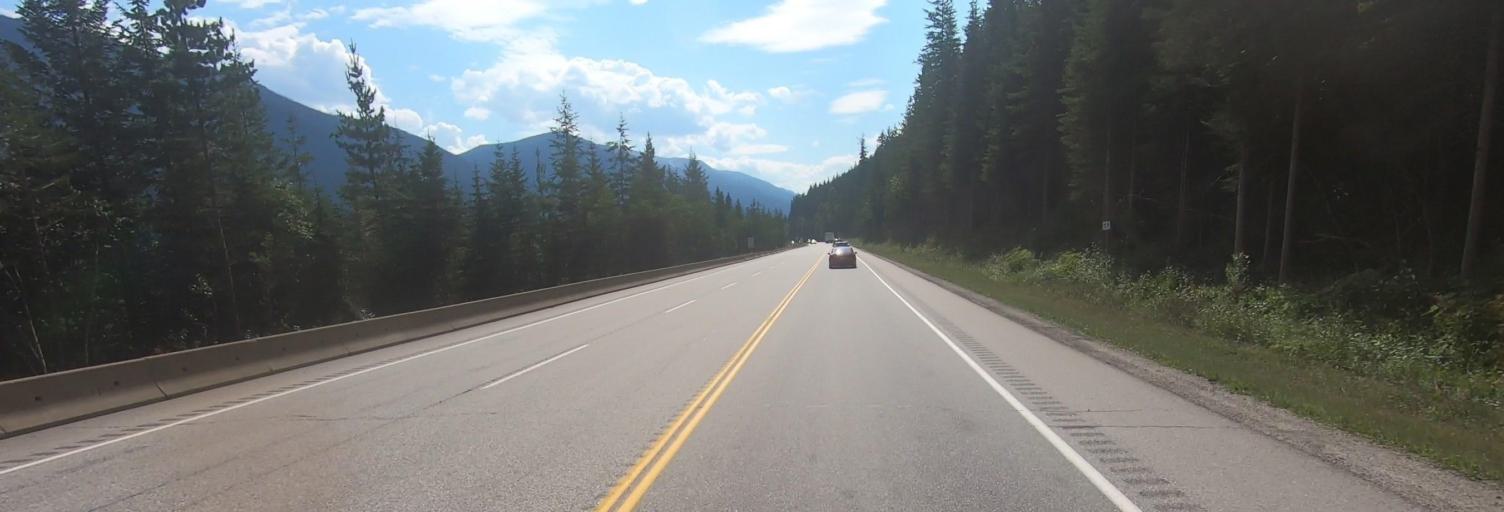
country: CA
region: British Columbia
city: Golden
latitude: 51.3729
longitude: -117.4491
